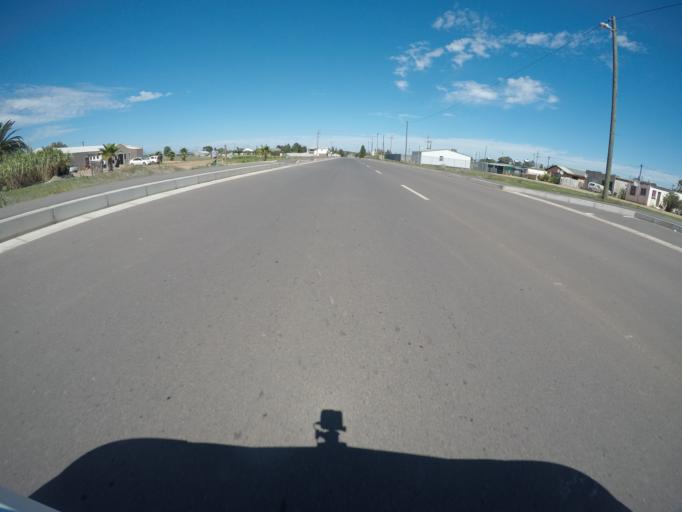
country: ZA
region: Western Cape
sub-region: West Coast District Municipality
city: Malmesbury
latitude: -33.5744
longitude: 18.6470
